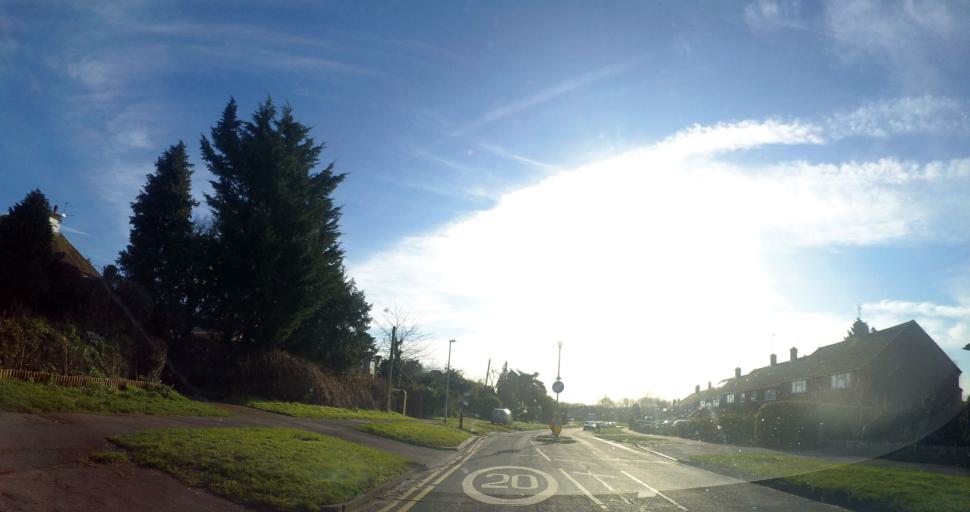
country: GB
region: England
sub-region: West Berkshire
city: Tilehurst
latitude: 51.4441
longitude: -1.0076
